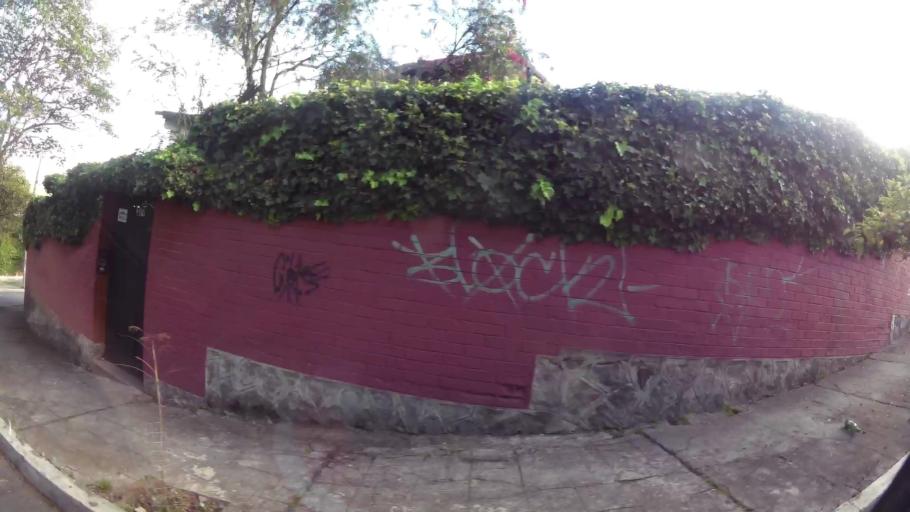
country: EC
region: Pichincha
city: Quito
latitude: -0.2057
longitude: -78.4801
